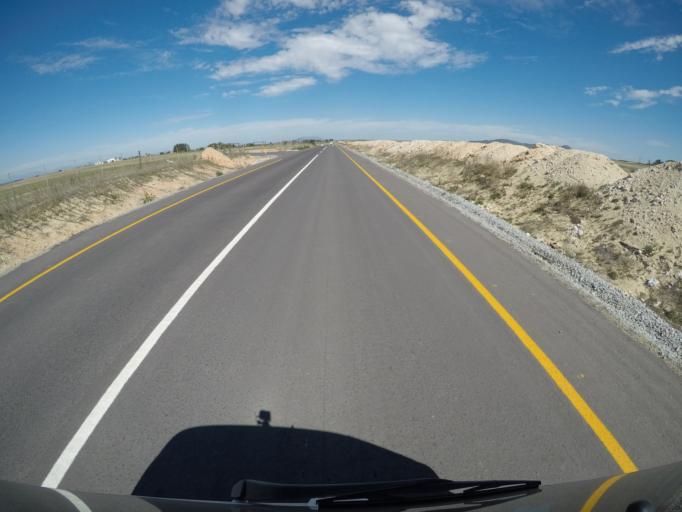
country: ZA
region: Western Cape
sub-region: West Coast District Municipality
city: Malmesbury
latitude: -33.5193
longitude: 18.6527
